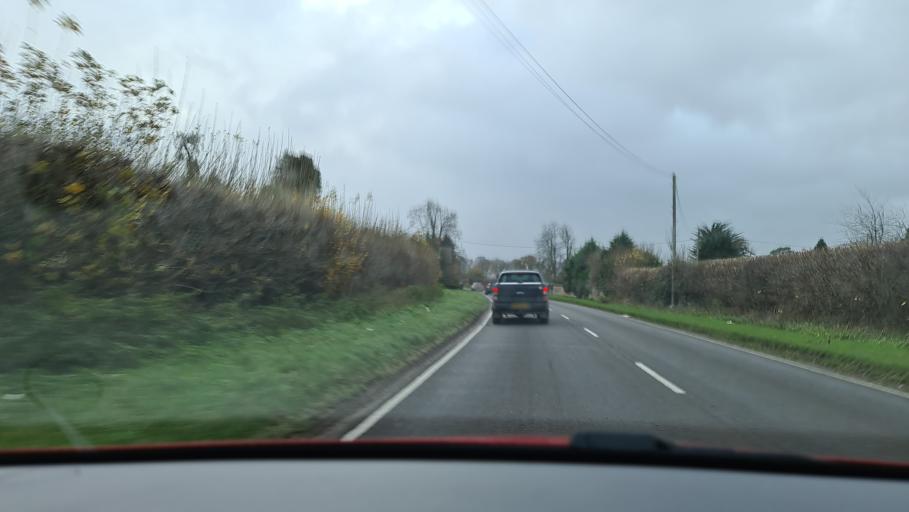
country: GB
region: England
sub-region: Buckinghamshire
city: Great Missenden
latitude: 51.7257
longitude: -0.7246
